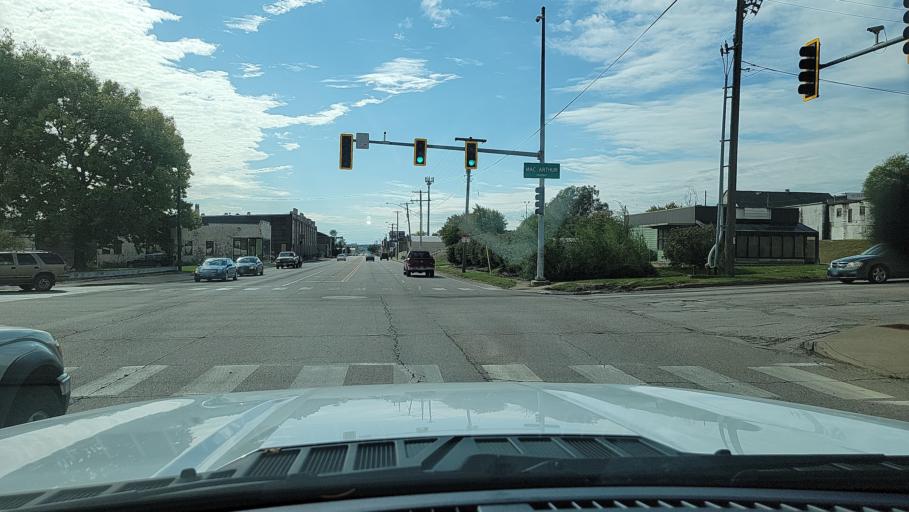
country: US
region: Illinois
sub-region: Peoria County
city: Peoria
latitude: 40.6810
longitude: -89.6041
